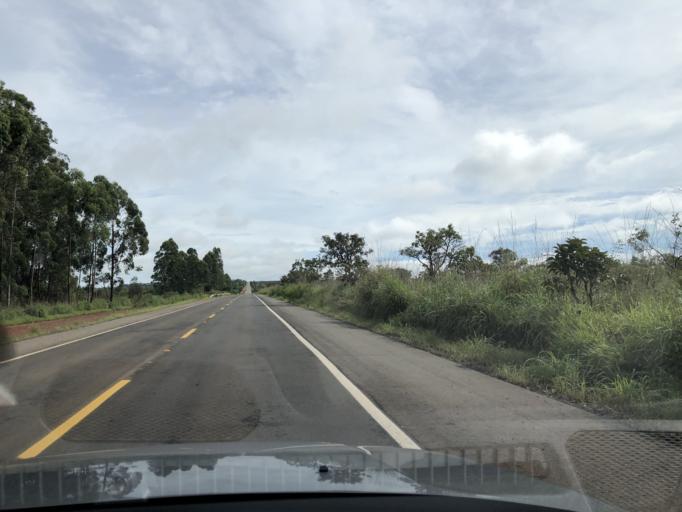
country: BR
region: Federal District
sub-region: Brasilia
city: Brasilia
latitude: -15.6734
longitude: -48.0885
